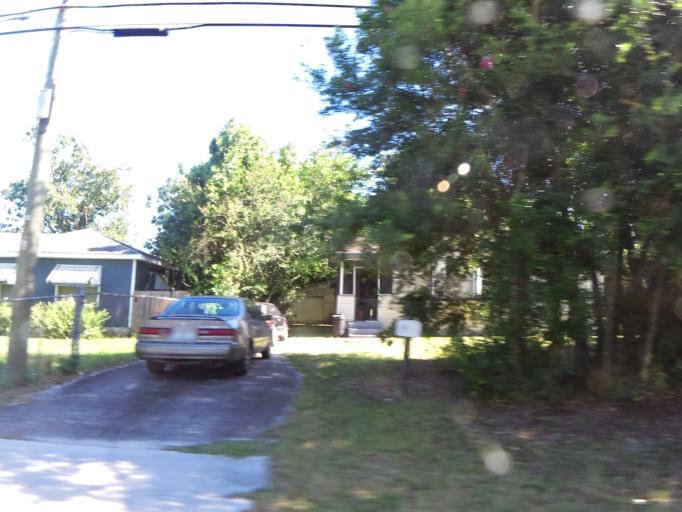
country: US
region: Florida
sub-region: Duval County
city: Jacksonville
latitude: 30.2755
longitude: -81.7225
